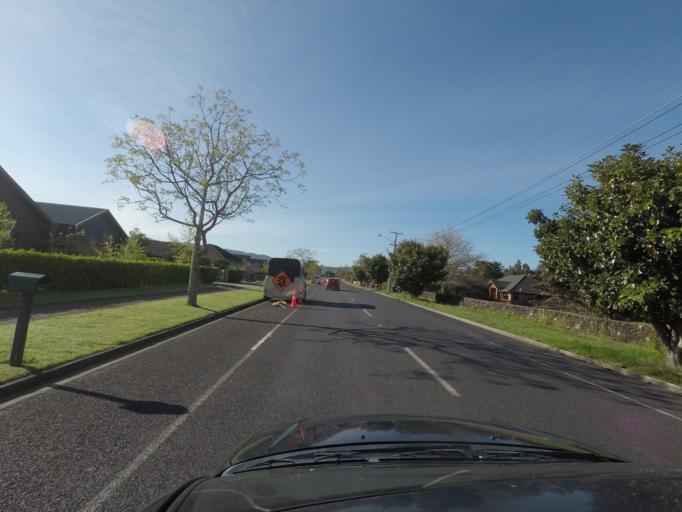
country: NZ
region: Auckland
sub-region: Auckland
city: Red Hill
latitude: -36.9974
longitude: 175.0379
